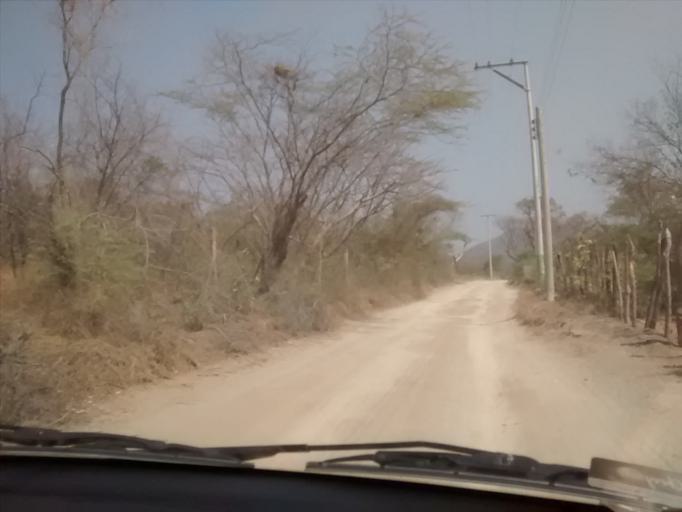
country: CO
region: Magdalena
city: Santa Marta
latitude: 11.1651
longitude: -74.2151
